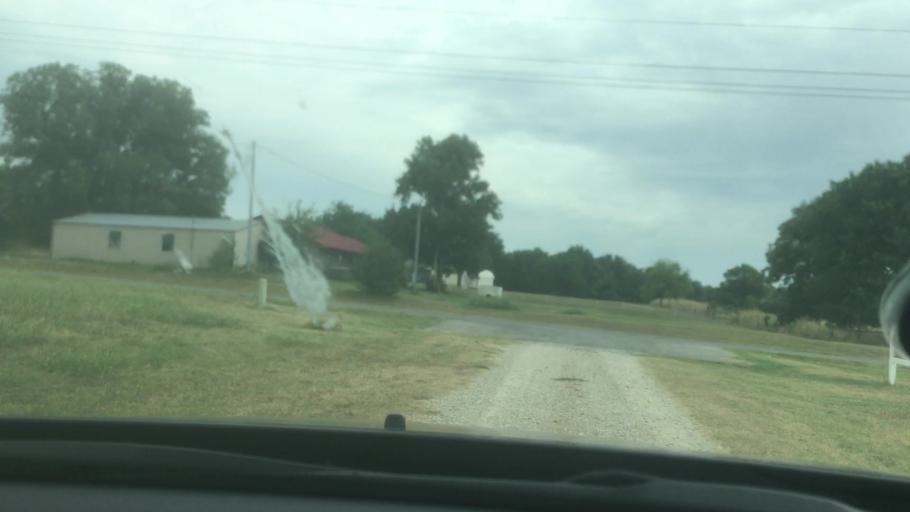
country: US
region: Oklahoma
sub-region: Murray County
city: Davis
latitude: 34.4776
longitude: -97.0588
